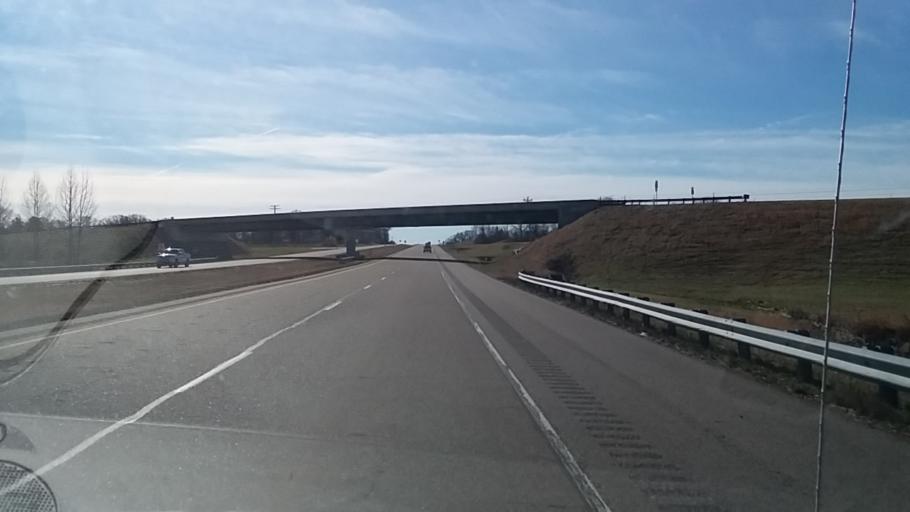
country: US
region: Tennessee
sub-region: Crockett County
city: Alamo
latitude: 35.8369
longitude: -89.1862
